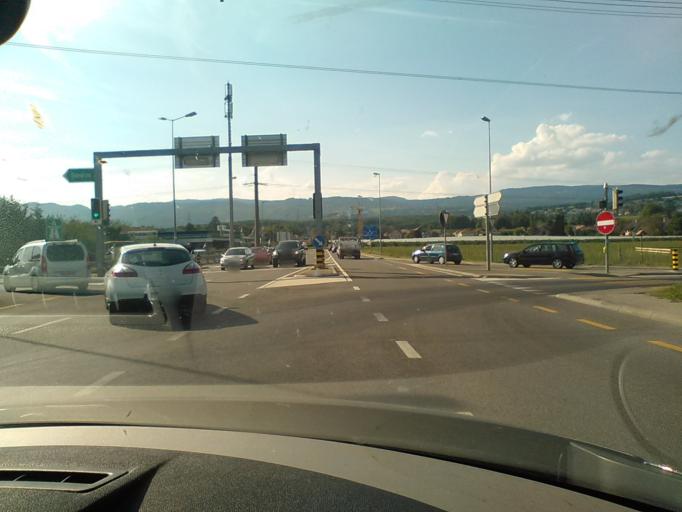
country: CH
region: Vaud
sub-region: Nyon District
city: Gland
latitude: 46.4249
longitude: 6.2572
